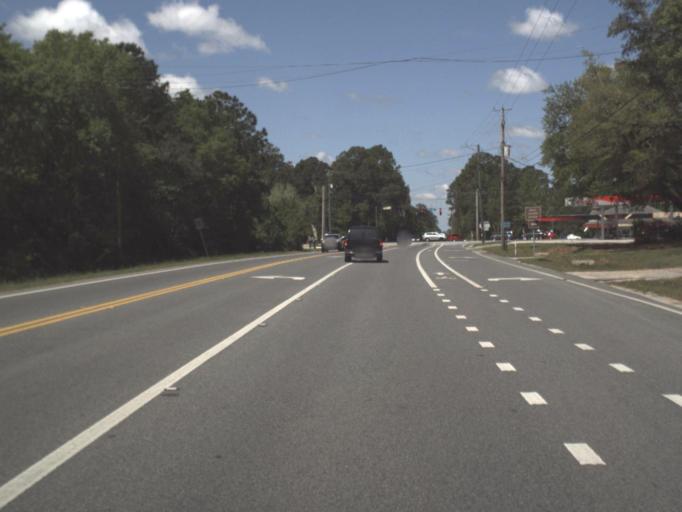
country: US
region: Florida
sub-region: Escambia County
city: Myrtle Grove
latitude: 30.4211
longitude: -87.3268
